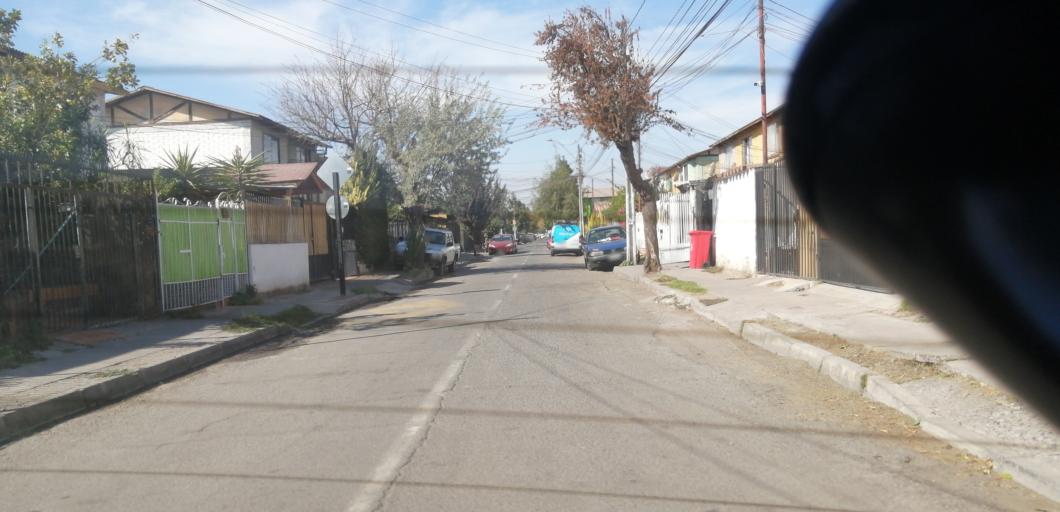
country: CL
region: Santiago Metropolitan
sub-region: Provincia de Santiago
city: Lo Prado
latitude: -33.4607
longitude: -70.7358
